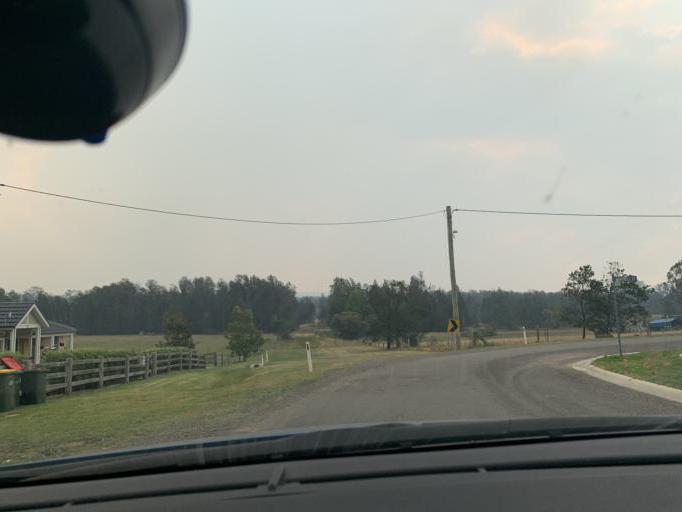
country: AU
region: New South Wales
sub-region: Cessnock
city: Cessnock
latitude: -32.9240
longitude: 151.3102
